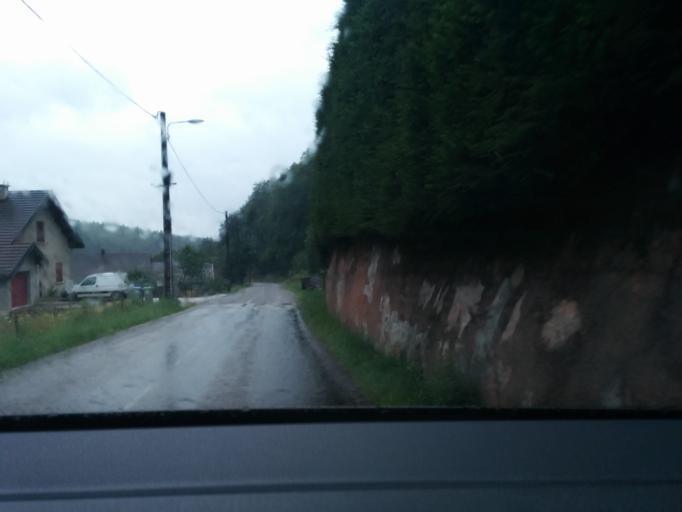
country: FR
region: Franche-Comte
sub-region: Departement du Jura
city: Valfin-les-Saint-Claude
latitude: 46.4507
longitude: 5.8262
